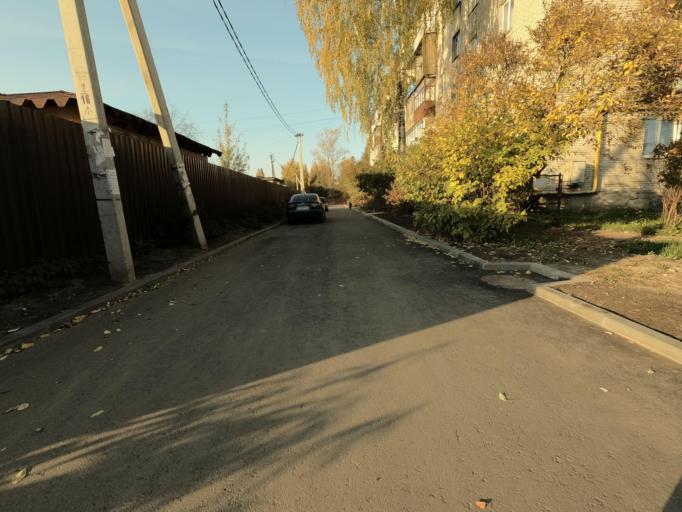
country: RU
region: Leningrad
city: Mga
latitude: 59.7591
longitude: 31.0685
